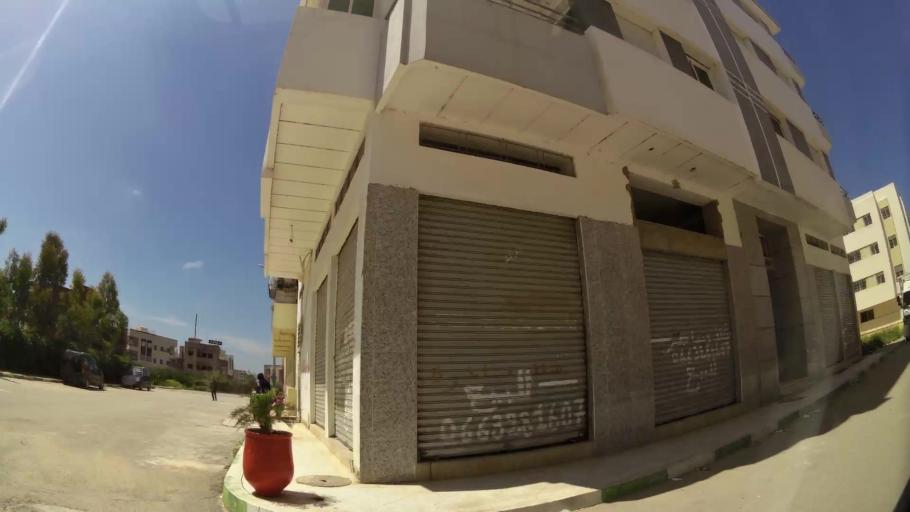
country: MA
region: Fes-Boulemane
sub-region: Fes
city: Fes
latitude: 34.0229
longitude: -5.0480
